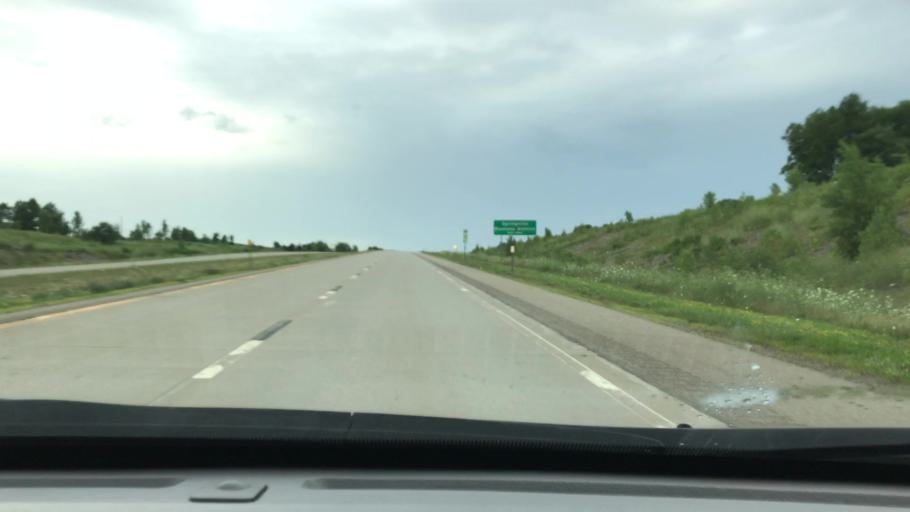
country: US
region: New York
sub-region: Erie County
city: Springville
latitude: 42.4934
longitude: -78.6968
